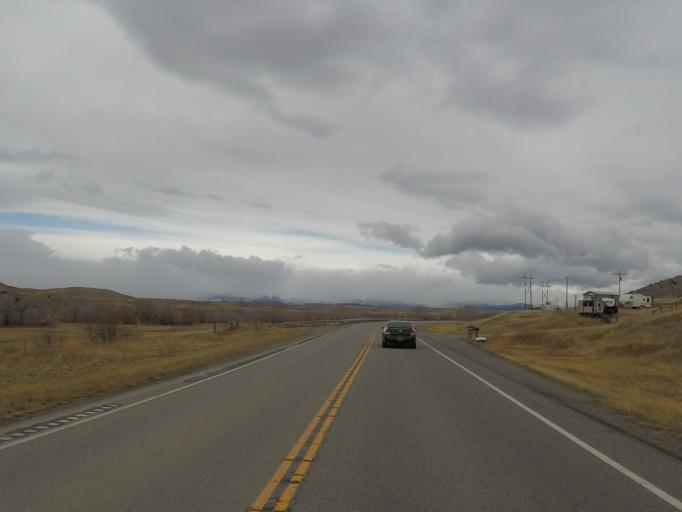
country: US
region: Montana
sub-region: Sweet Grass County
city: Big Timber
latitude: 45.8692
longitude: -109.9434
